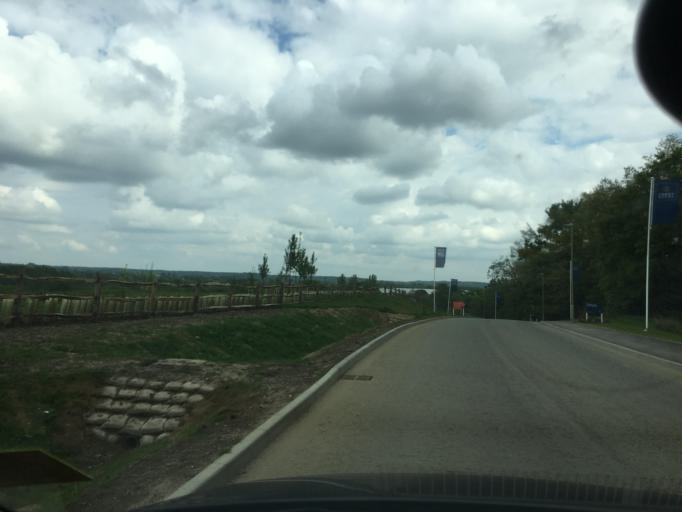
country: GB
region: England
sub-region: Surrey
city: Frimley
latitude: 51.3191
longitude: -0.7716
